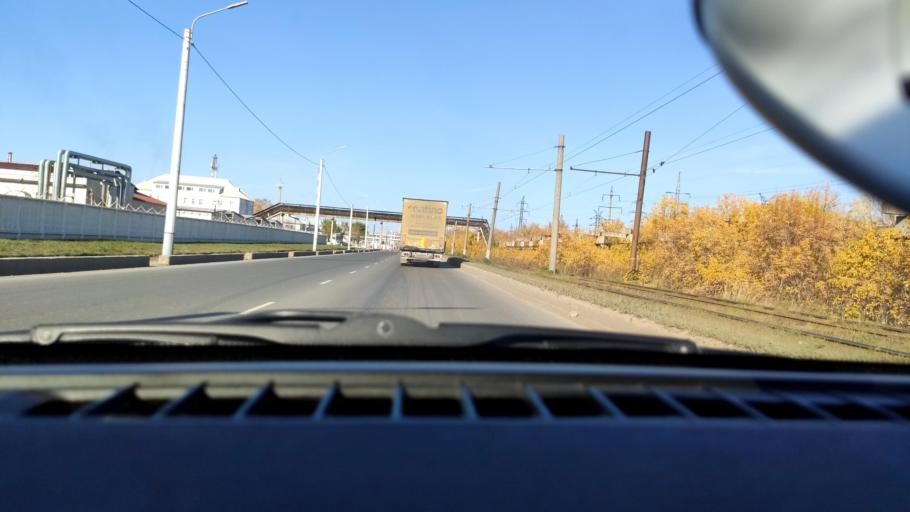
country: RU
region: Perm
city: Gamovo
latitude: 57.9199
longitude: 56.1460
